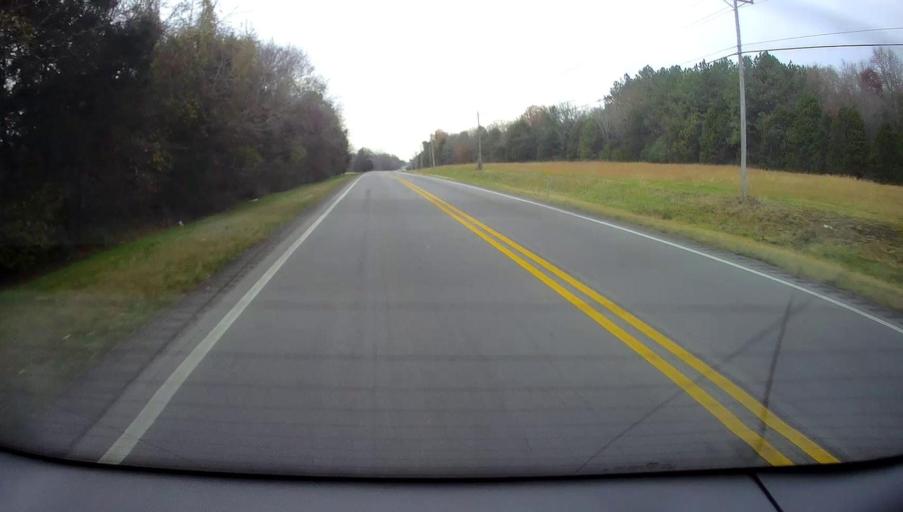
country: US
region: Alabama
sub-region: Morgan County
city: Priceville
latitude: 34.4357
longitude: -86.7396
